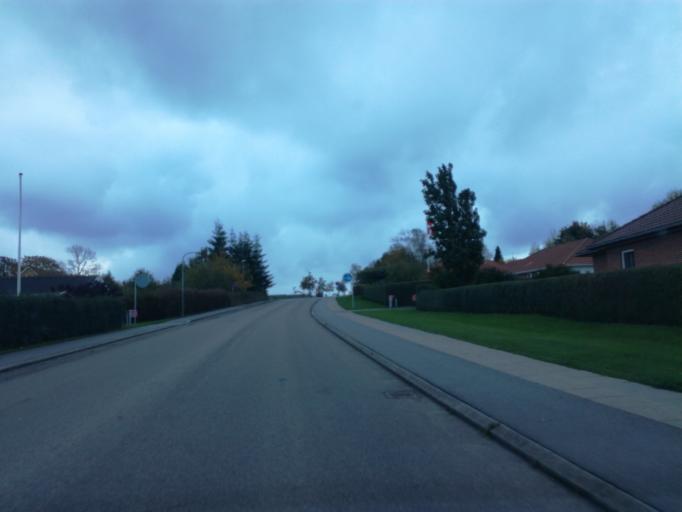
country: DK
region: South Denmark
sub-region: Vejle Kommune
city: Borkop
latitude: 55.6347
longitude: 9.6540
